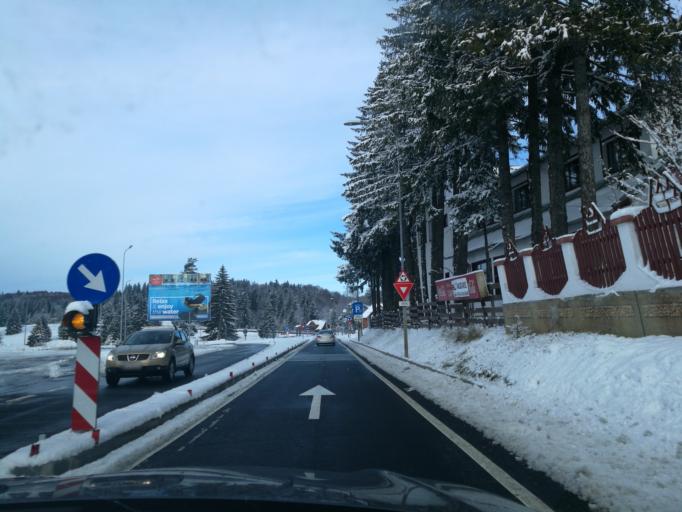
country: RO
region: Brasov
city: Brasov
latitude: 45.6085
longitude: 25.5540
